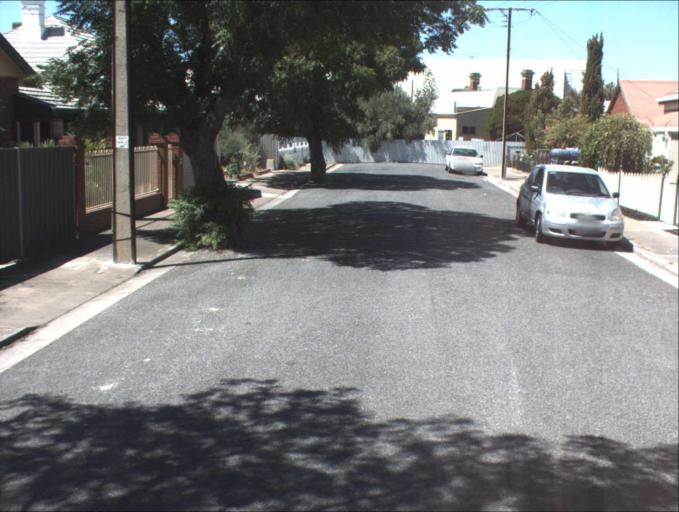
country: AU
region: South Australia
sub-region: Port Adelaide Enfield
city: Birkenhead
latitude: -34.8365
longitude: 138.4990
